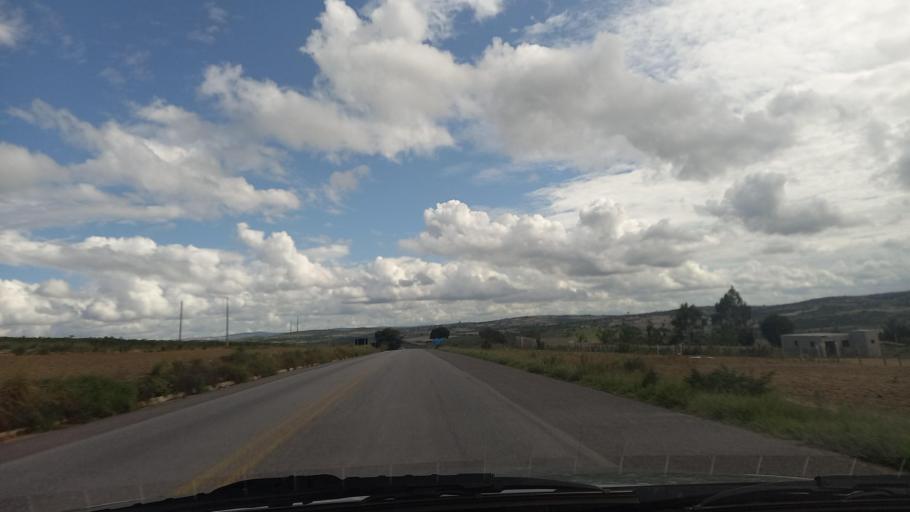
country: BR
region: Pernambuco
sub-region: Lajedo
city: Lajedo
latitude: -8.7225
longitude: -36.4273
